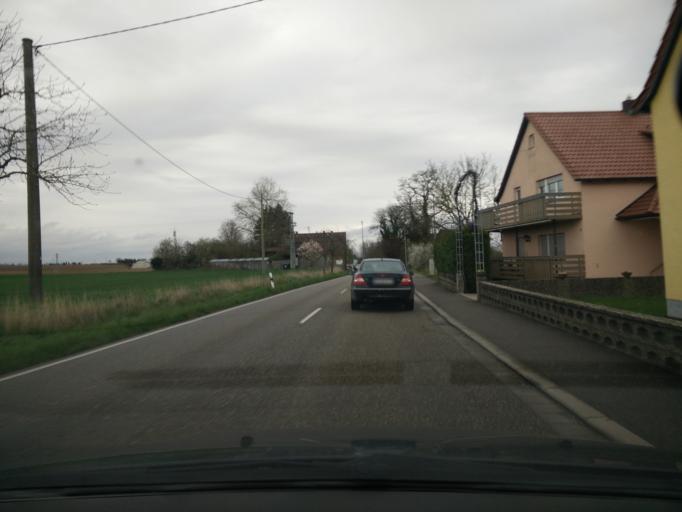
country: DE
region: Rheinland-Pfalz
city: Vollmersweiler
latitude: 49.0559
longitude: 8.0646
